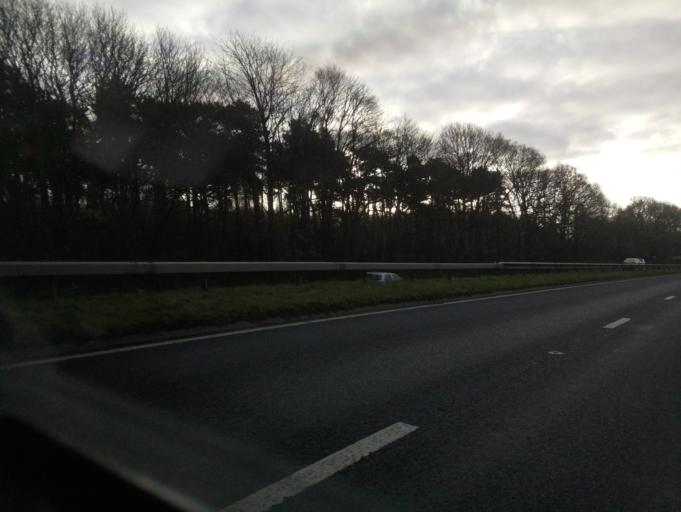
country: GB
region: England
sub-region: Staffordshire
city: Shenstone
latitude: 52.6078
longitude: -1.7951
